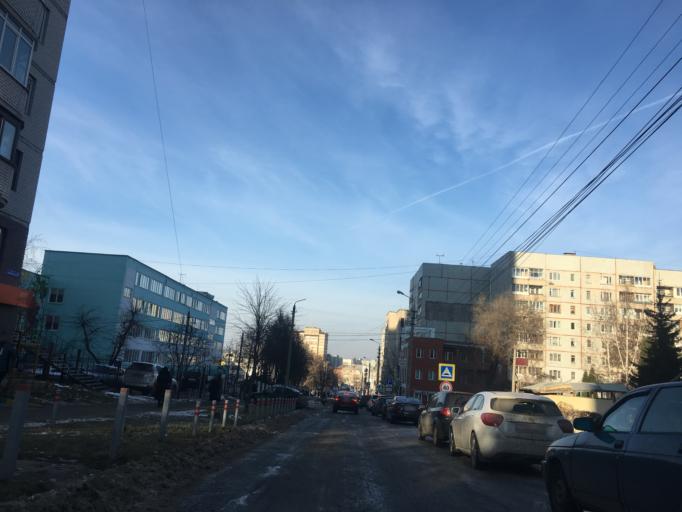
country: RU
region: Tula
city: Tula
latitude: 54.1942
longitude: 37.5882
